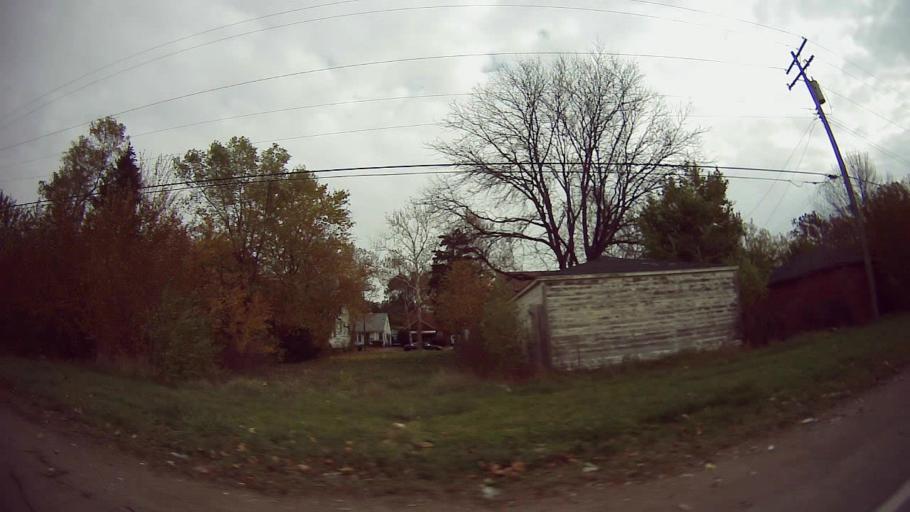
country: US
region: Michigan
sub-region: Wayne County
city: Hamtramck
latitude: 42.4143
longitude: -83.0424
